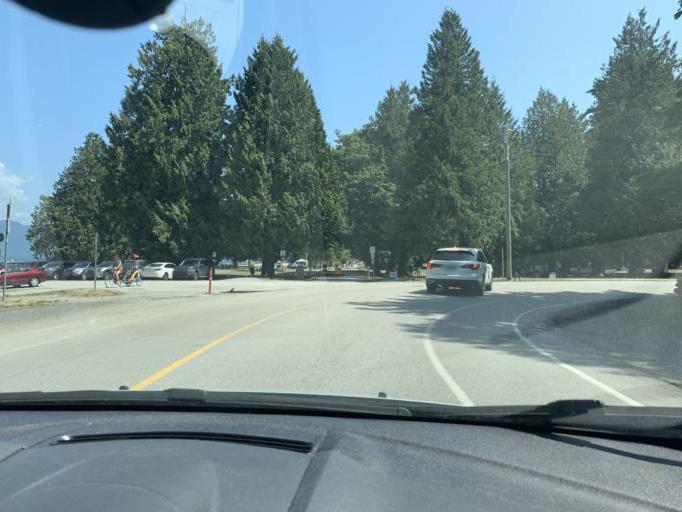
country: CA
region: British Columbia
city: West End
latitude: 49.2748
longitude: -123.2060
